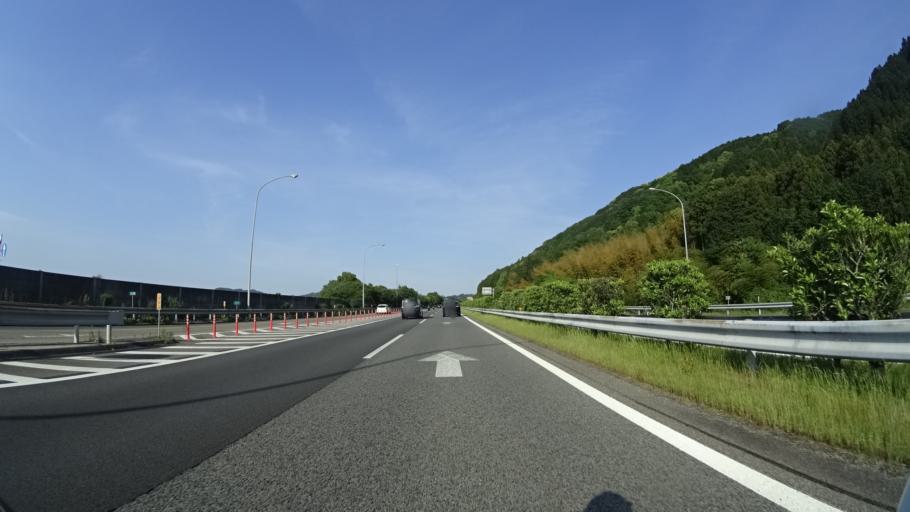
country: JP
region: Ehime
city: Niihama
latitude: 33.9275
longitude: 133.3299
